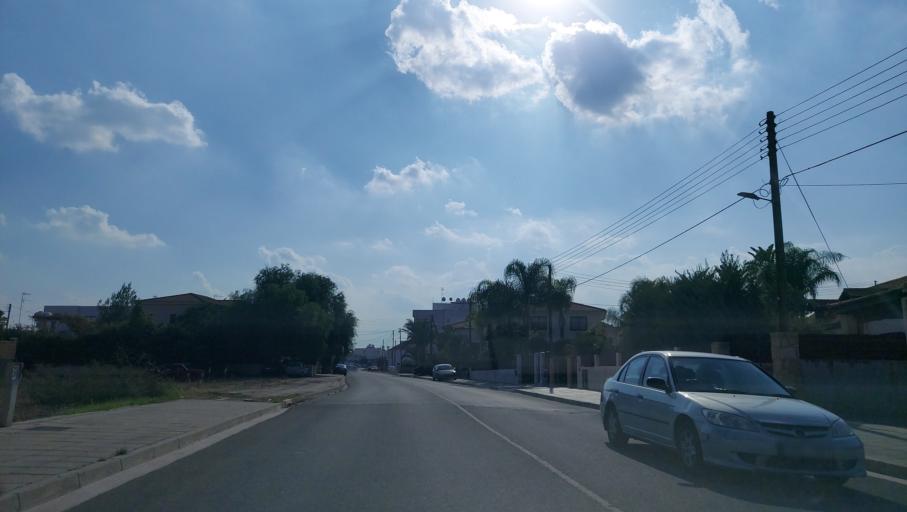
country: CY
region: Lefkosia
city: Tseri
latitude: 35.1046
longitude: 33.3076
